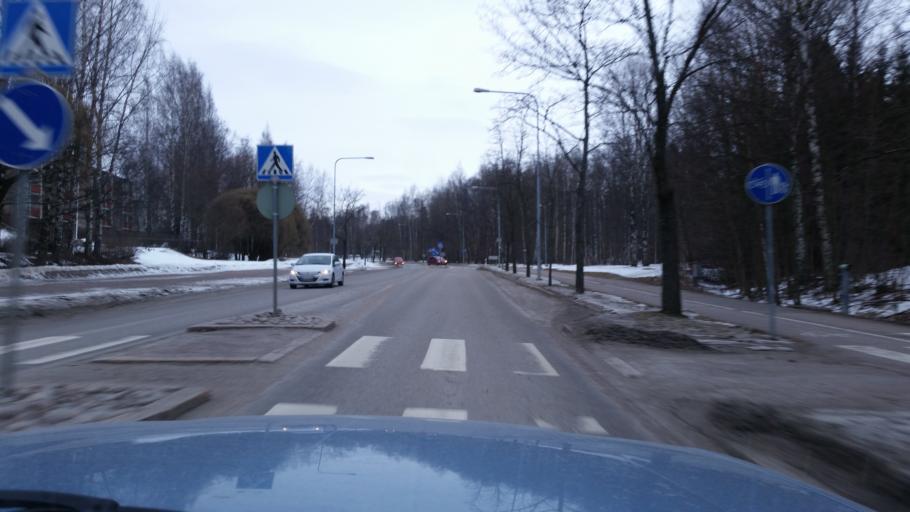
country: FI
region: Uusimaa
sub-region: Helsinki
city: Helsinki
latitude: 60.2239
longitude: 24.9666
